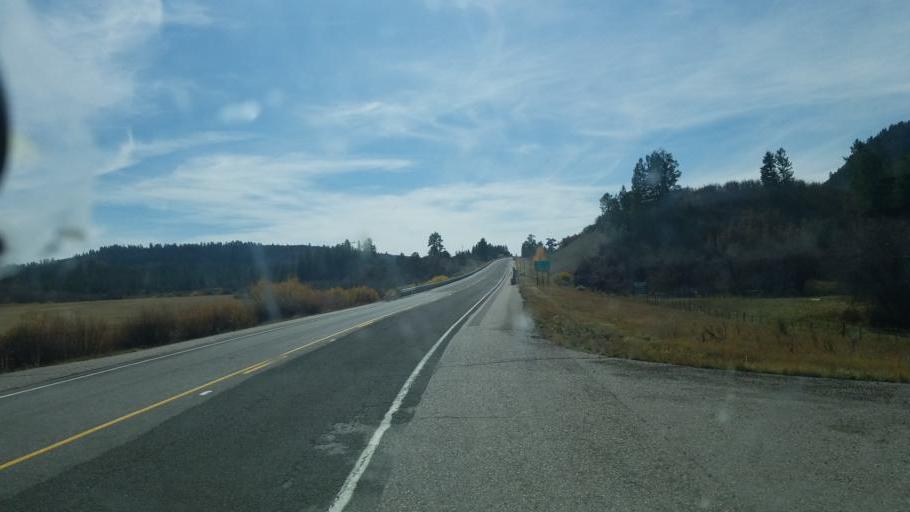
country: US
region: New Mexico
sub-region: Rio Arriba County
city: Chama
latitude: 36.9911
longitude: -106.7811
